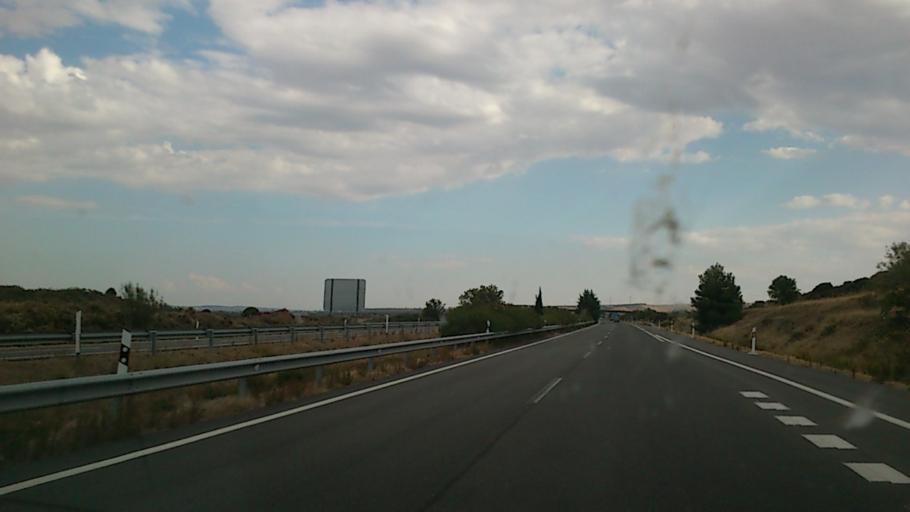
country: ES
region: La Rioja
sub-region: Provincia de La Rioja
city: Pradejon
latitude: 42.3588
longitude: -2.0642
